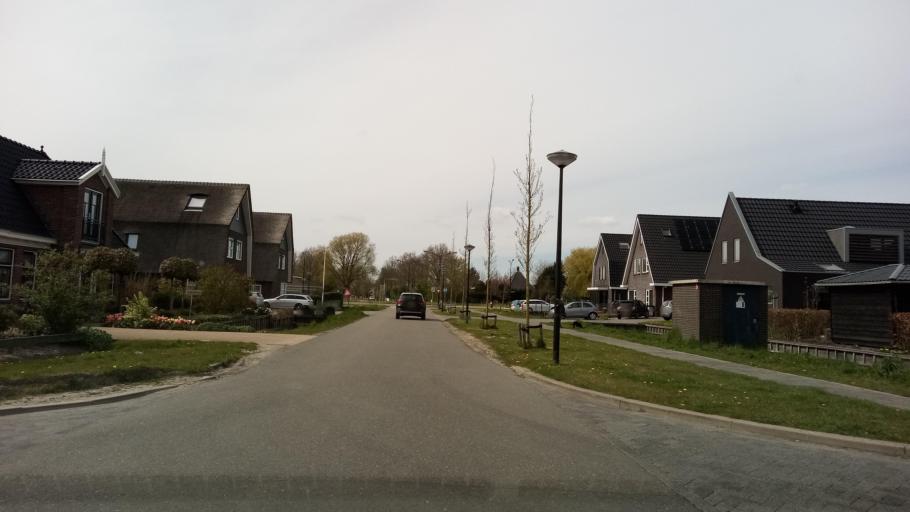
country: NL
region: North Holland
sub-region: Gemeente Heerhugowaard
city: Heerhugowaard
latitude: 52.6672
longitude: 4.8613
